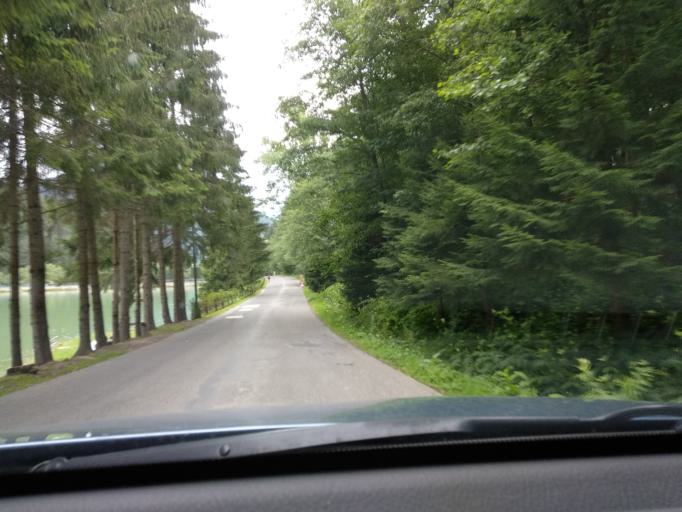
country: SK
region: Zilinsky
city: Ruzomberok
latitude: 49.0711
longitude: 19.2736
